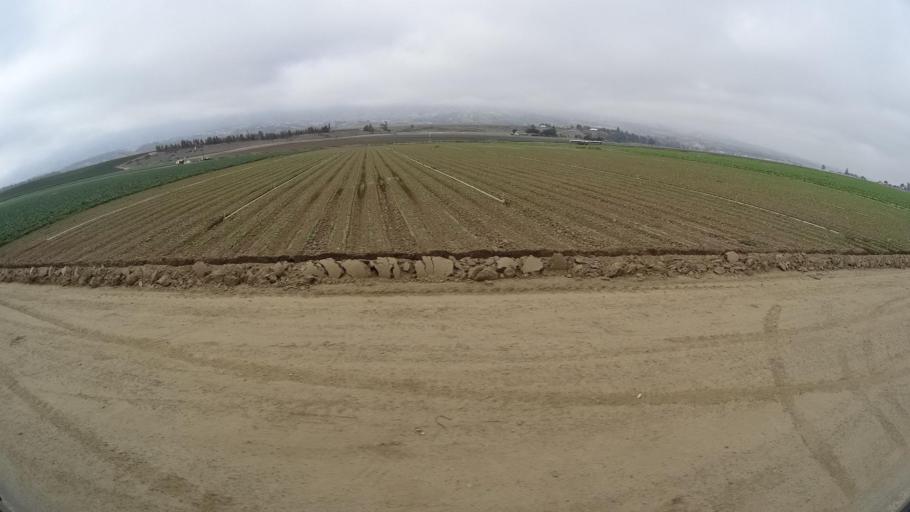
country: US
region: California
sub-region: Monterey County
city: Soledad
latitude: 36.3788
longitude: -121.3287
